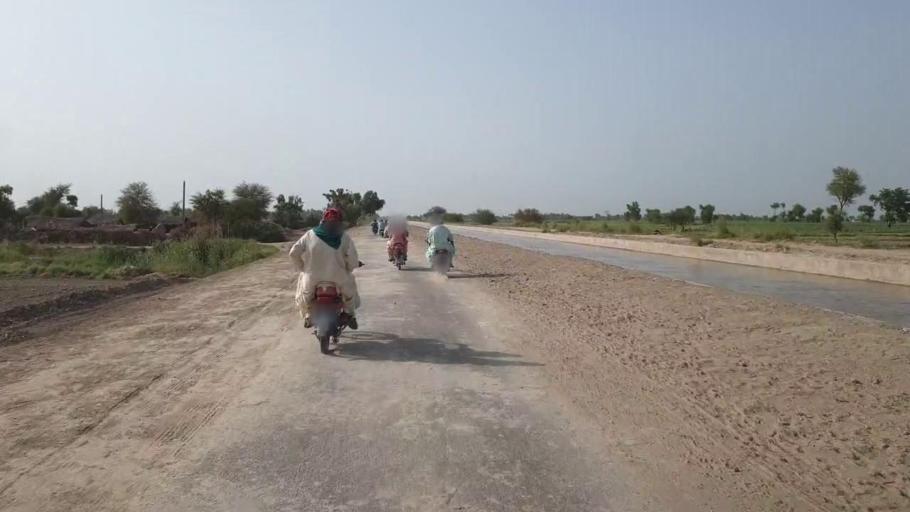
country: PK
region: Sindh
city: Daur
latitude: 26.3395
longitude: 68.1632
